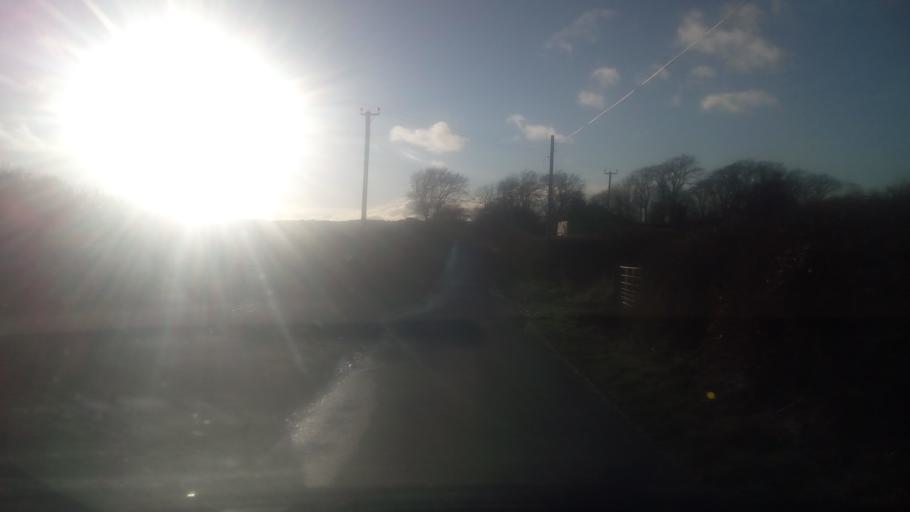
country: GB
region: Scotland
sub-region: The Scottish Borders
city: Jedburgh
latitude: 55.4703
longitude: -2.4699
